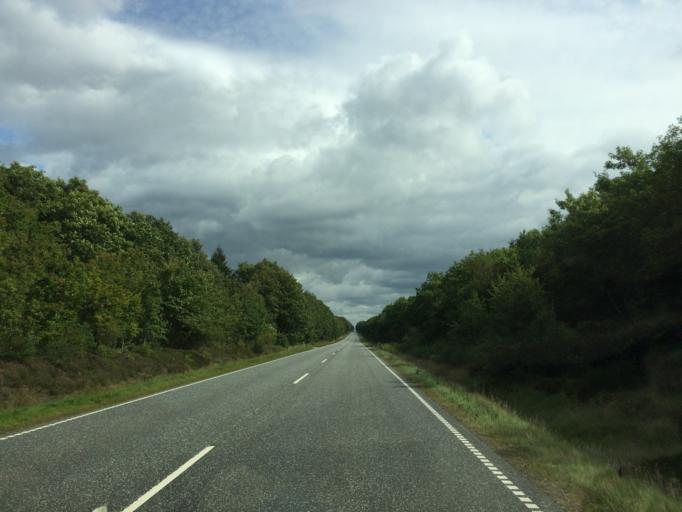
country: DK
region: Central Jutland
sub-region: Holstebro Kommune
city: Vinderup
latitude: 56.3940
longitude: 8.8432
